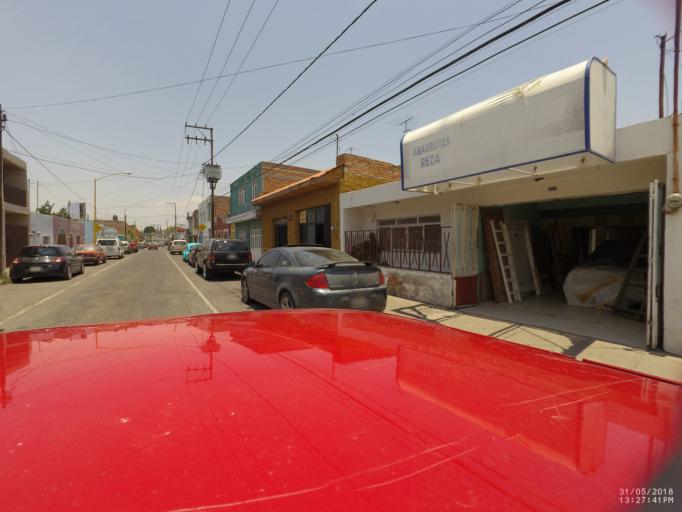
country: MX
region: Aguascalientes
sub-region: Aguascalientes
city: Aguascalientes
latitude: 21.8803
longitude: -102.3110
